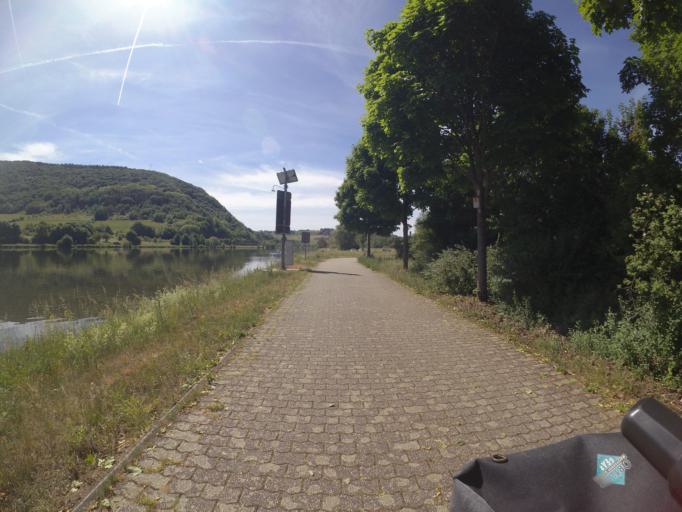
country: DE
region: Rheinland-Pfalz
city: Schoden
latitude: 49.6344
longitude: 6.5729
